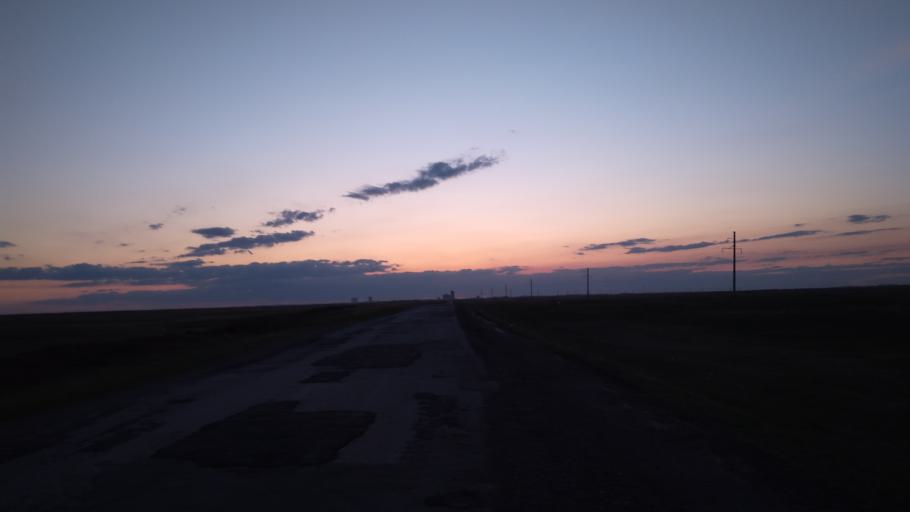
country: RU
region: Chelyabinsk
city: Troitsk
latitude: 54.0883
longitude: 61.6536
